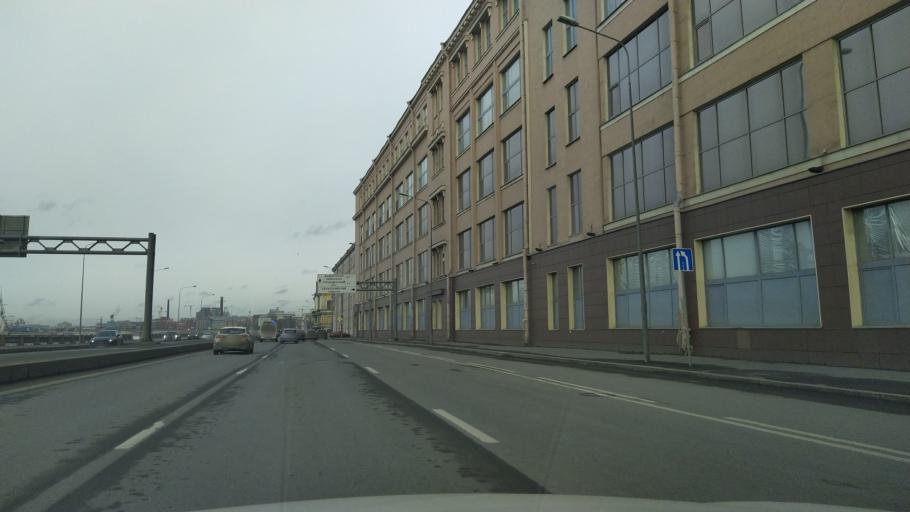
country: RU
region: Leningrad
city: Sampsonievskiy
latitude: 59.9616
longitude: 30.3383
